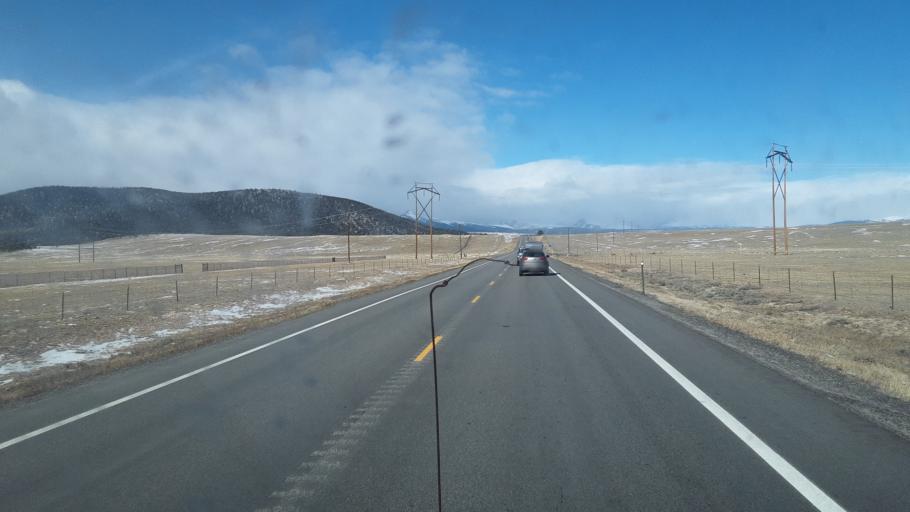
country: US
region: Colorado
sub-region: Park County
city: Fairplay
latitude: 39.0832
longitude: -105.9771
